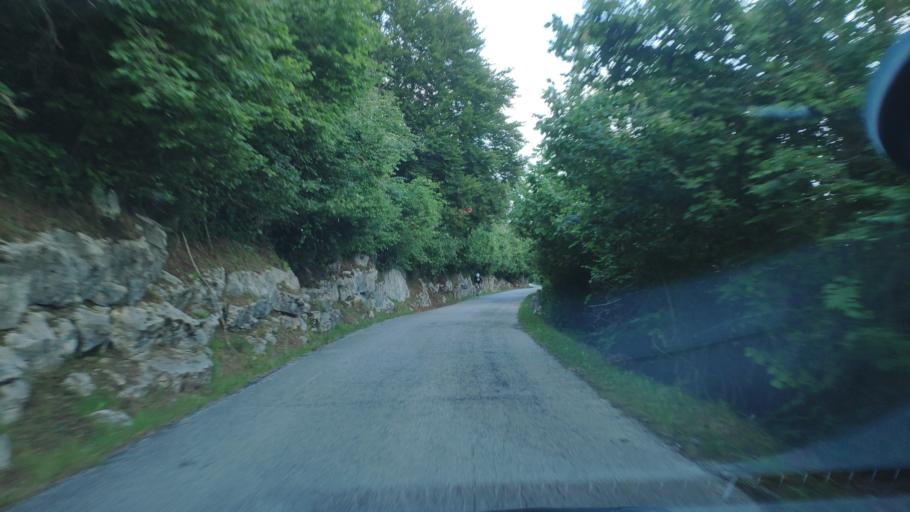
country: IT
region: Veneto
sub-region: Provincia di Vicenza
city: Calvene
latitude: 45.7902
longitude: 11.5163
